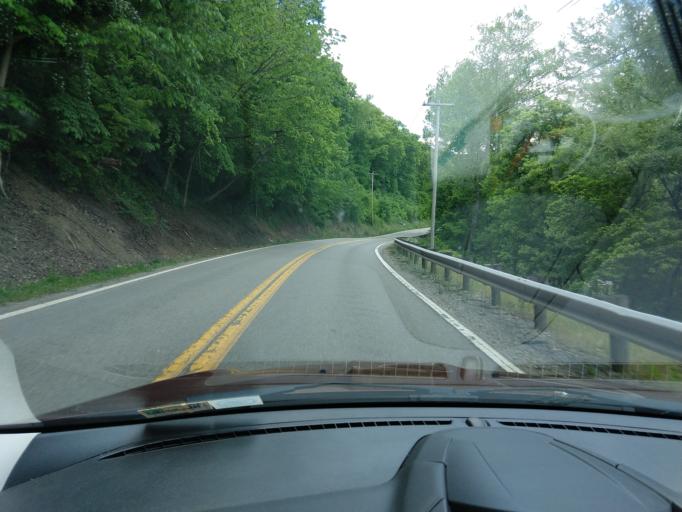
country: US
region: West Virginia
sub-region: Gilmer County
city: Glenville
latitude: 38.8647
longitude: -80.6966
